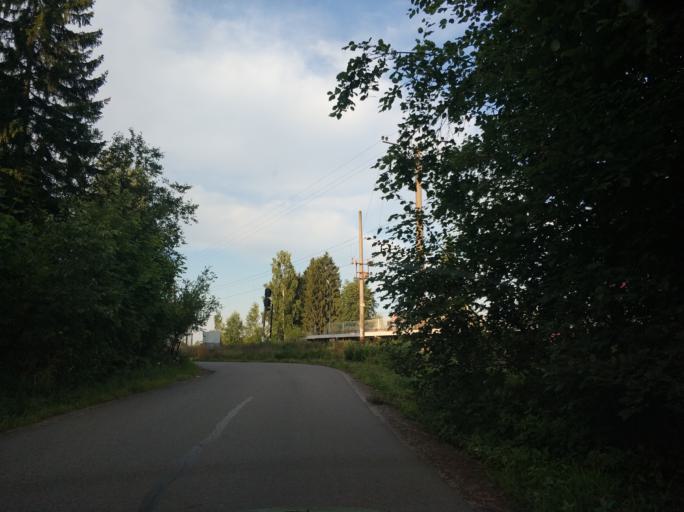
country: RU
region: Leningrad
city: Shcheglovo
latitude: 60.0543
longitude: 30.7447
